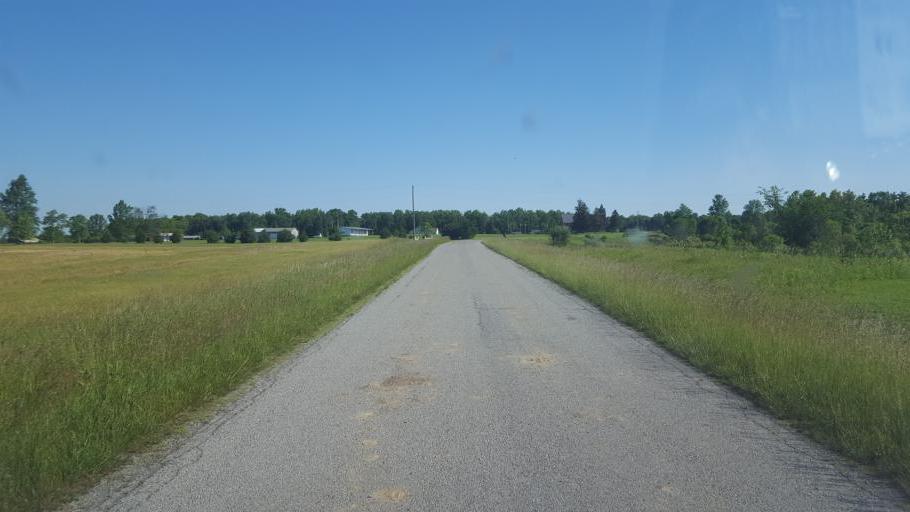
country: US
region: Ohio
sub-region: Crawford County
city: Bucyrus
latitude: 40.7404
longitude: -82.9161
